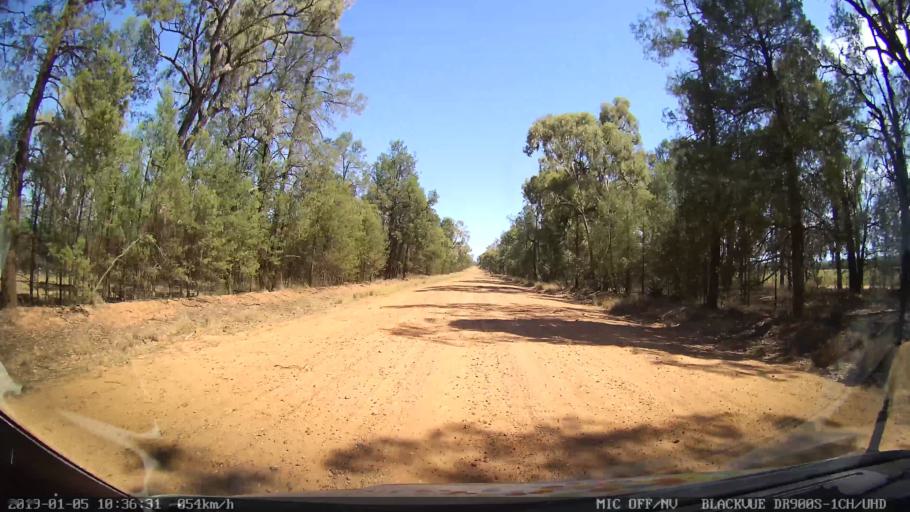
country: AU
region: New South Wales
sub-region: Gilgandra
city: Gilgandra
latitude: -31.4815
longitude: 148.9248
